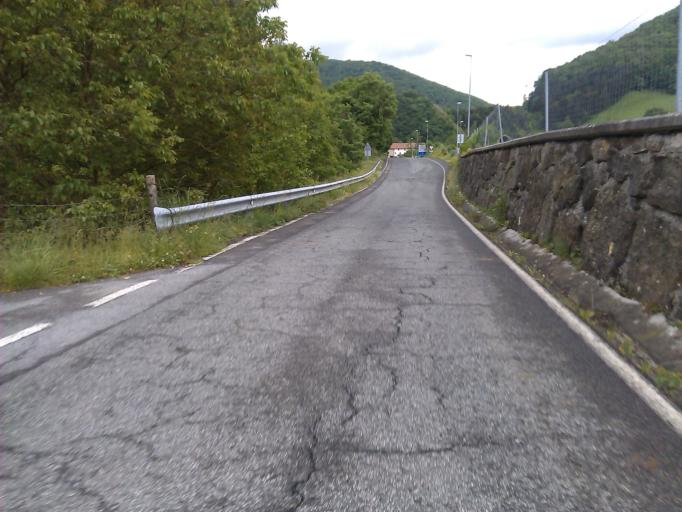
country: ES
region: Navarre
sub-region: Provincia de Navarra
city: Irurtzun
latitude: 42.9640
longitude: -1.8335
